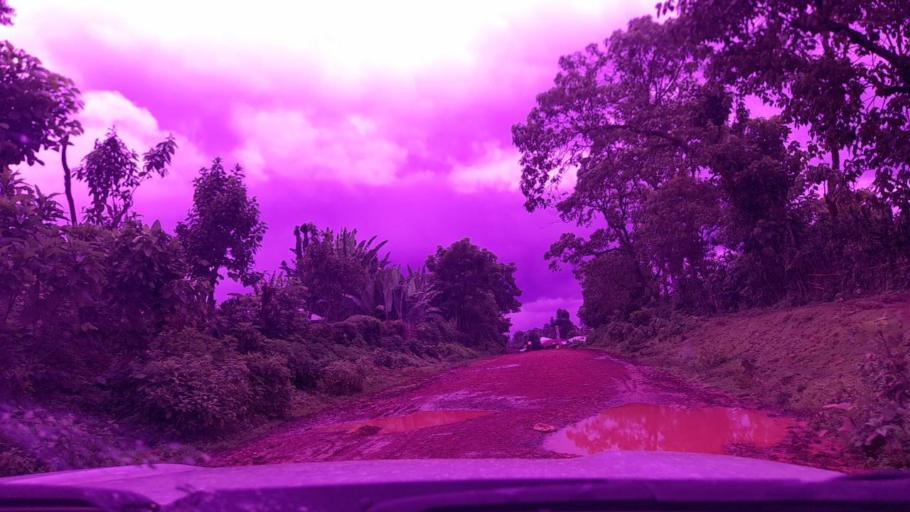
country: ET
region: Southern Nations, Nationalities, and People's Region
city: Tippi
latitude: 7.5782
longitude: 35.6332
